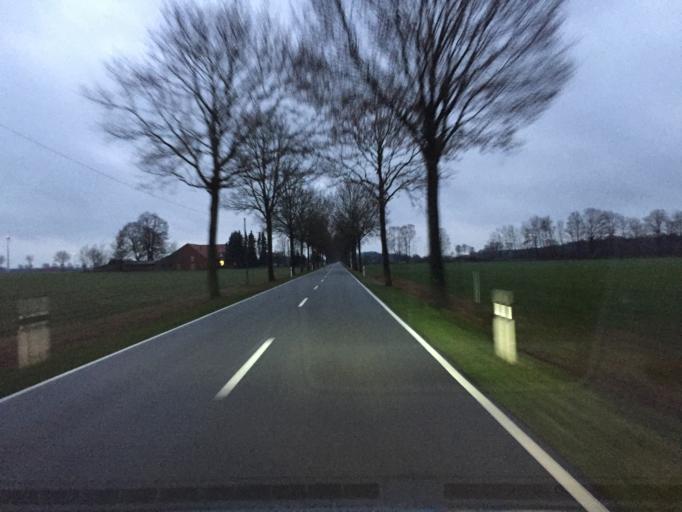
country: DE
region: Lower Saxony
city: Schwaforden
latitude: 52.7667
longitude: 8.8317
